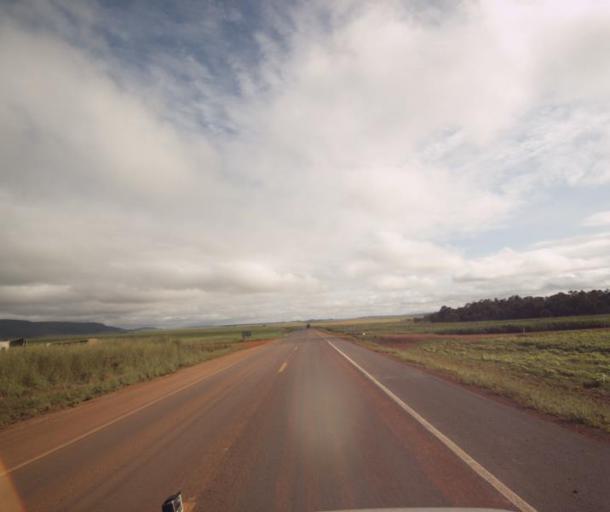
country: BR
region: Goias
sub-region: Padre Bernardo
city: Padre Bernardo
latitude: -15.4207
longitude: -48.6235
